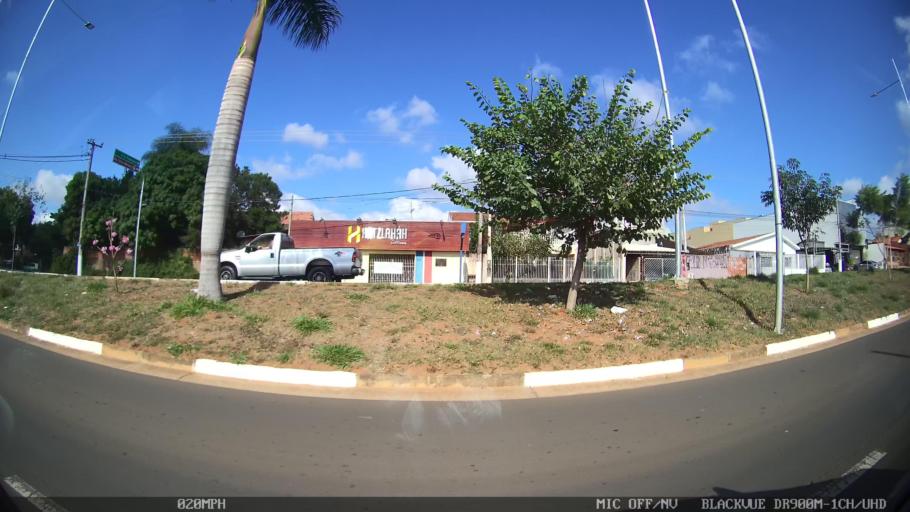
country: BR
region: Sao Paulo
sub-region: Hortolandia
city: Hortolandia
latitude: -22.8690
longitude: -47.2217
